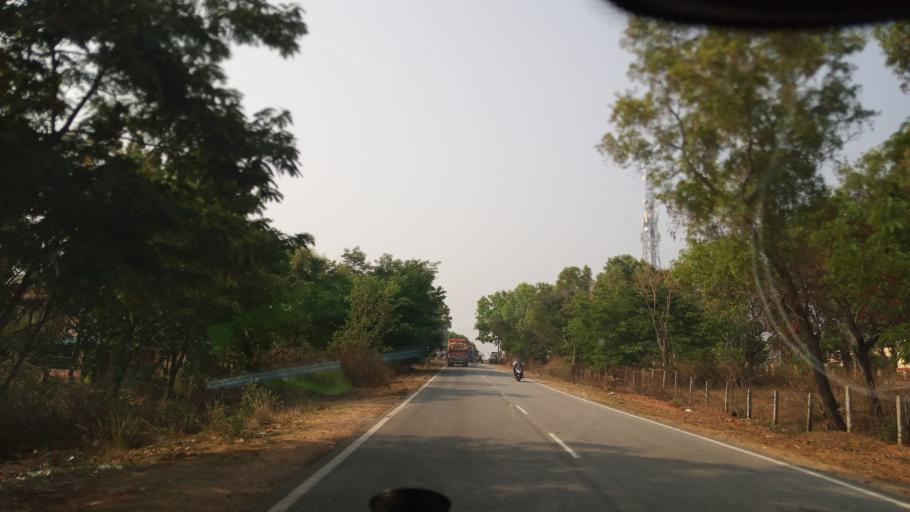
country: IN
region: Karnataka
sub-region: Mandya
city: Belluru
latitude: 12.9474
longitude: 76.7516
